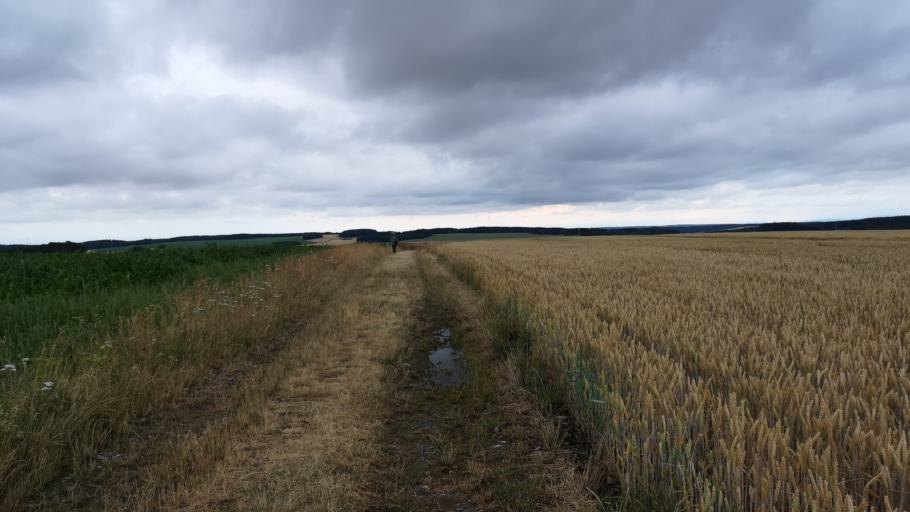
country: DE
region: Thuringia
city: Tanna
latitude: 50.4864
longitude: 11.8424
